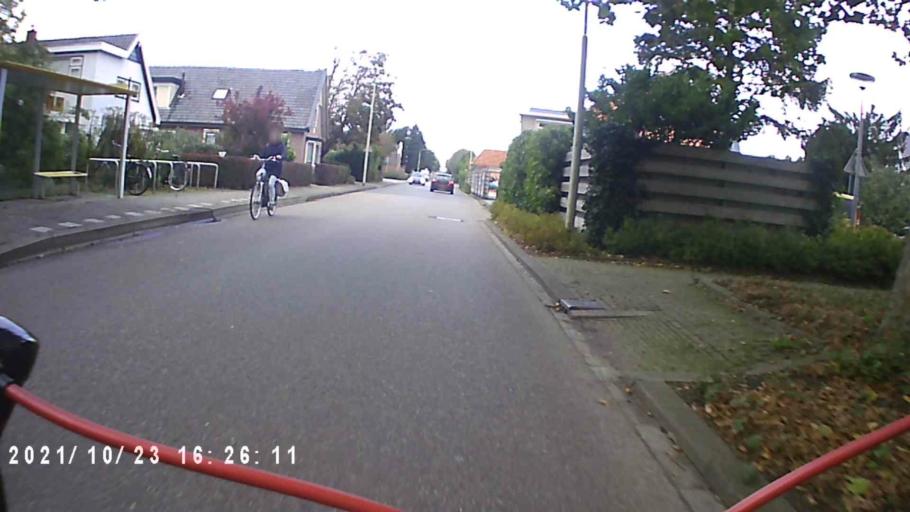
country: NL
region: North Holland
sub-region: Gemeente Langedijk
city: Broek op Langedijk
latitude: 52.7032
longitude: 4.8110
